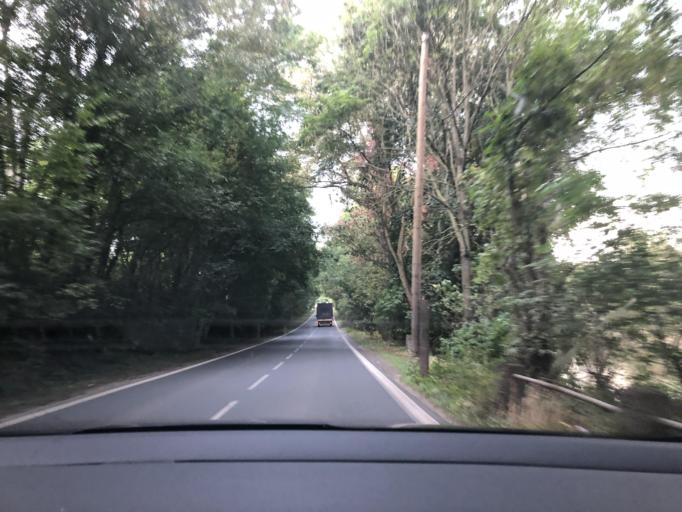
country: CZ
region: Central Bohemia
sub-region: Okres Kolin
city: Tynec nad Labem
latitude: 50.0356
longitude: 15.3557
